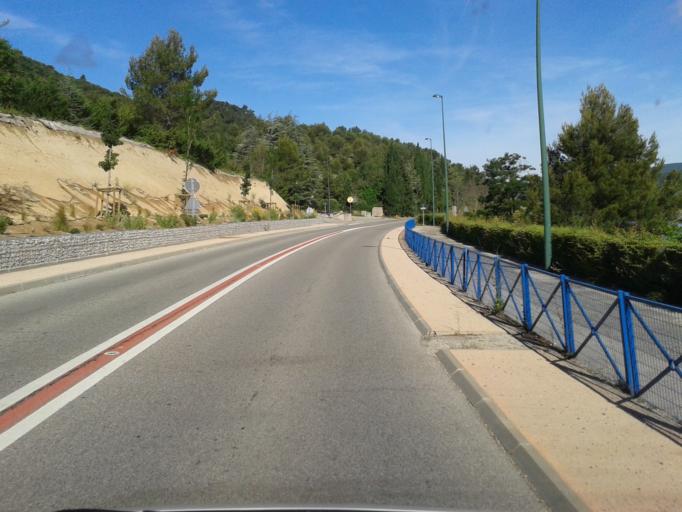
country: FR
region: Provence-Alpes-Cote d'Azur
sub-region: Departement du Vaucluse
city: Beaumont-de-Pertuis
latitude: 43.6859
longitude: 5.7052
